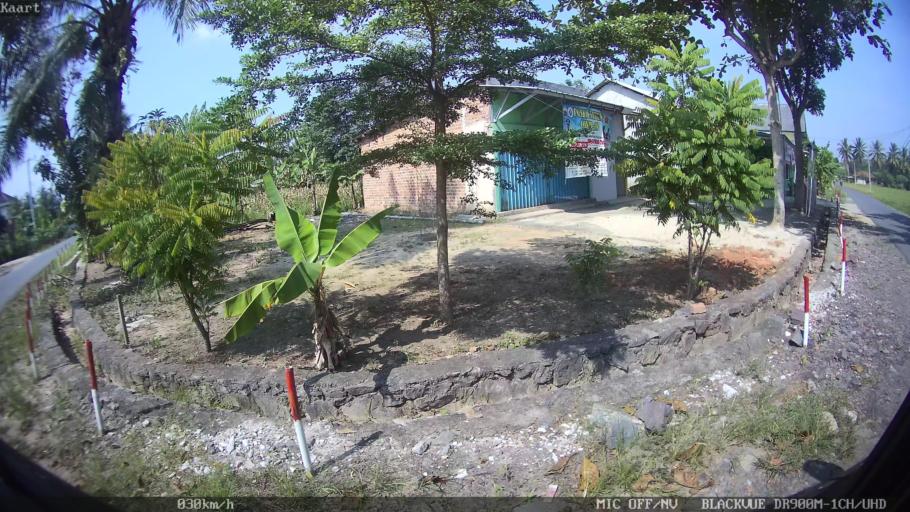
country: ID
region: Lampung
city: Natar
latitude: -5.2568
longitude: 105.2127
